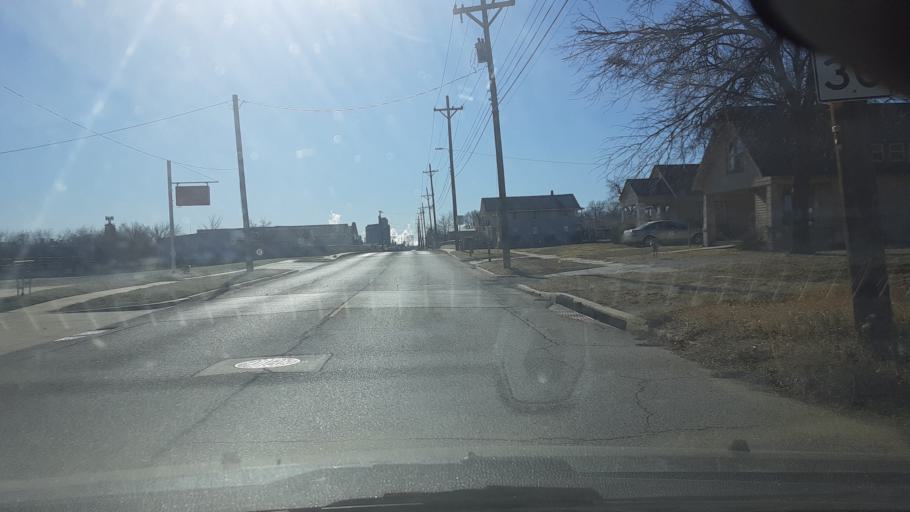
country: US
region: Oklahoma
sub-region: Kay County
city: Ponca City
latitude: 36.7107
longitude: -97.0853
